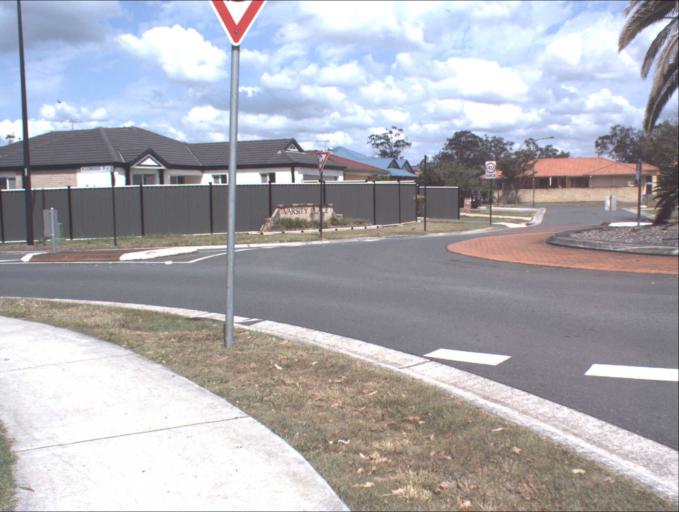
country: AU
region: Queensland
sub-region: Logan
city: Slacks Creek
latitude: -27.6608
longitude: 153.1436
